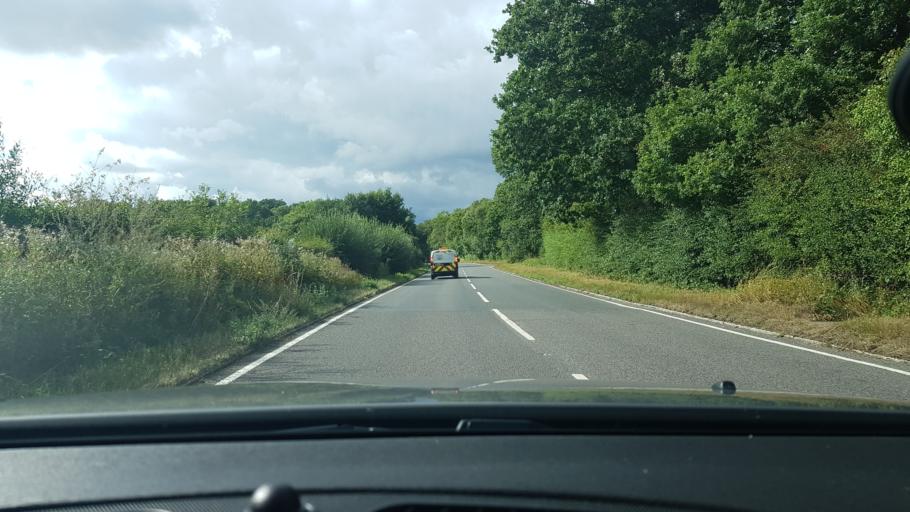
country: GB
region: England
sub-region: West Berkshire
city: Wickham
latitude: 51.4299
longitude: -1.4088
